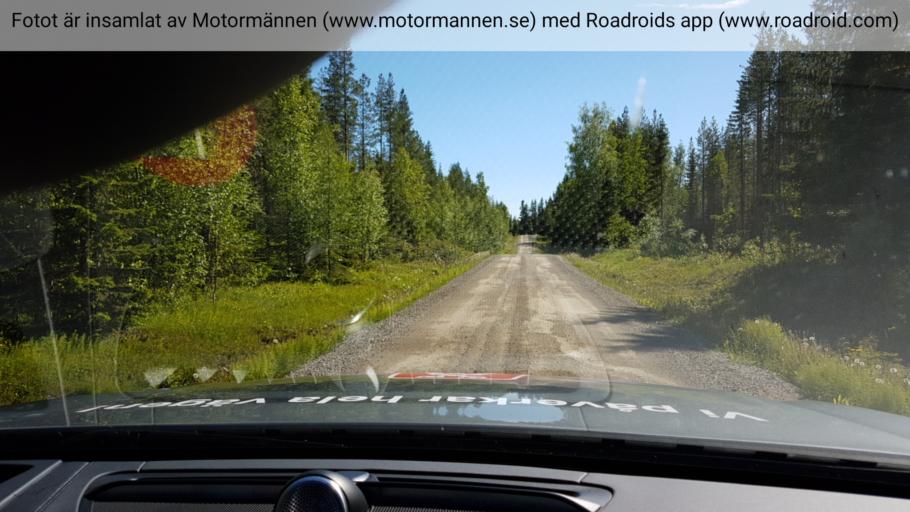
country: SE
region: Jaemtland
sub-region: Bergs Kommun
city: Hoverberg
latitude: 62.9114
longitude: 14.6352
